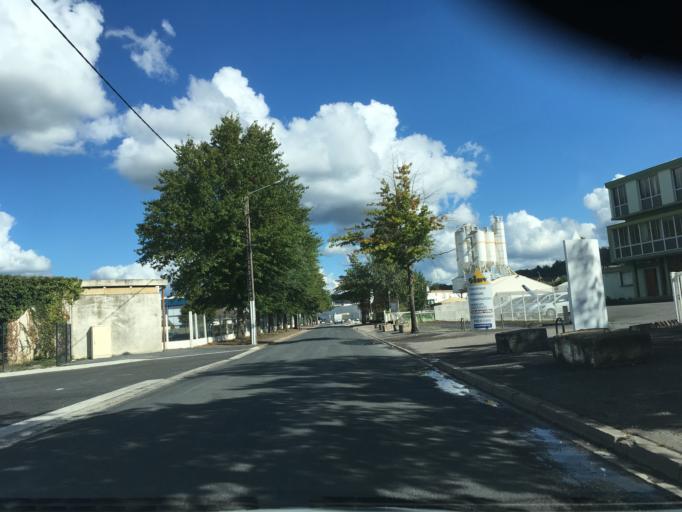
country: FR
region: Limousin
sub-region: Departement de la Correze
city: Brive-la-Gaillarde
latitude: 45.1510
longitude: 1.4919
